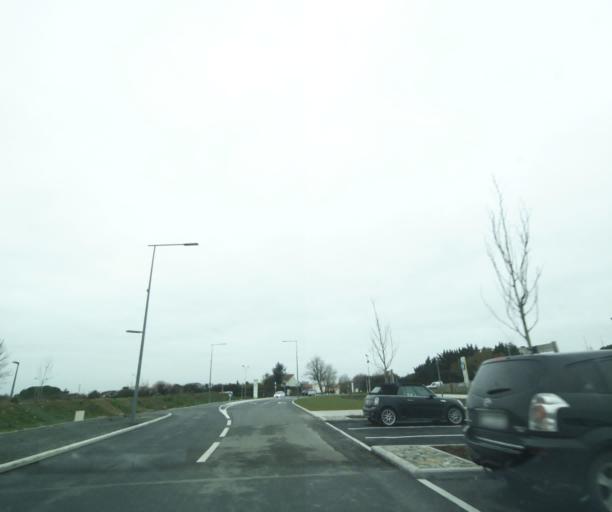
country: FR
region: Poitou-Charentes
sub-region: Departement de la Charente-Maritime
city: Lagord
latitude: 46.1832
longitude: -1.1512
